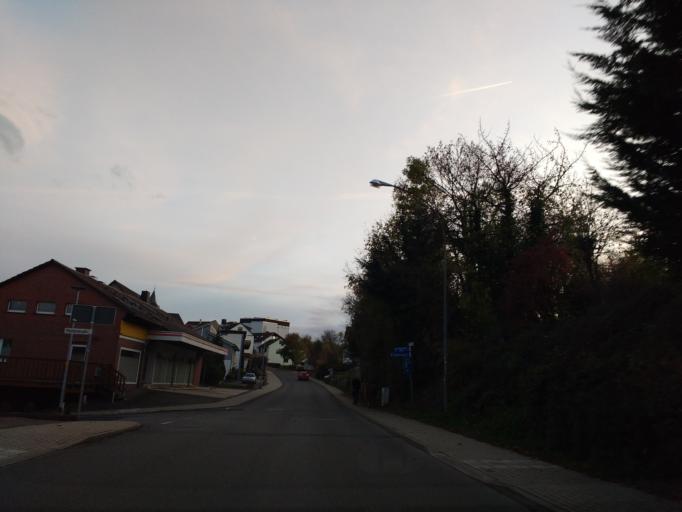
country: DE
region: Hesse
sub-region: Regierungsbezirk Kassel
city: Waldeck
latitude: 51.2090
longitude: 9.0608
